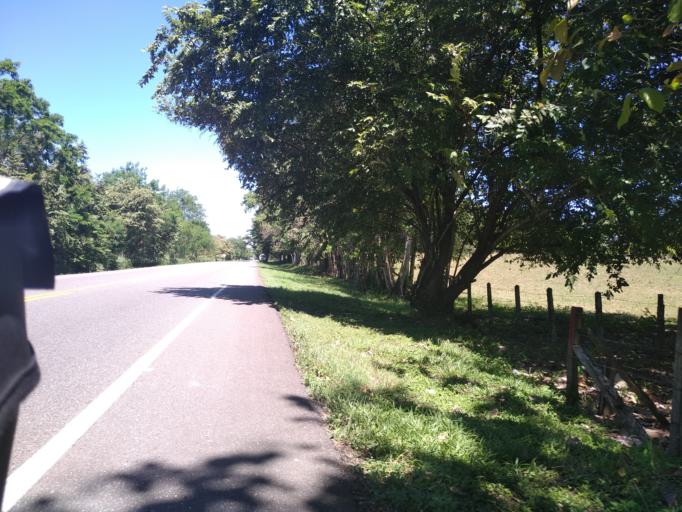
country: CO
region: Caldas
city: La Dorada
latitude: 5.3672
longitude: -74.7195
